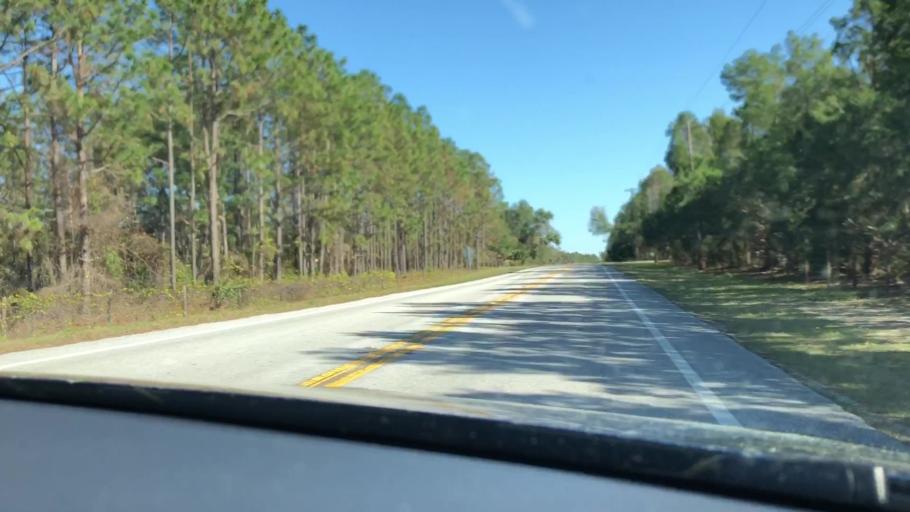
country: US
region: Florida
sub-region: Lake County
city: Eustis
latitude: 28.8720
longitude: -81.6312
